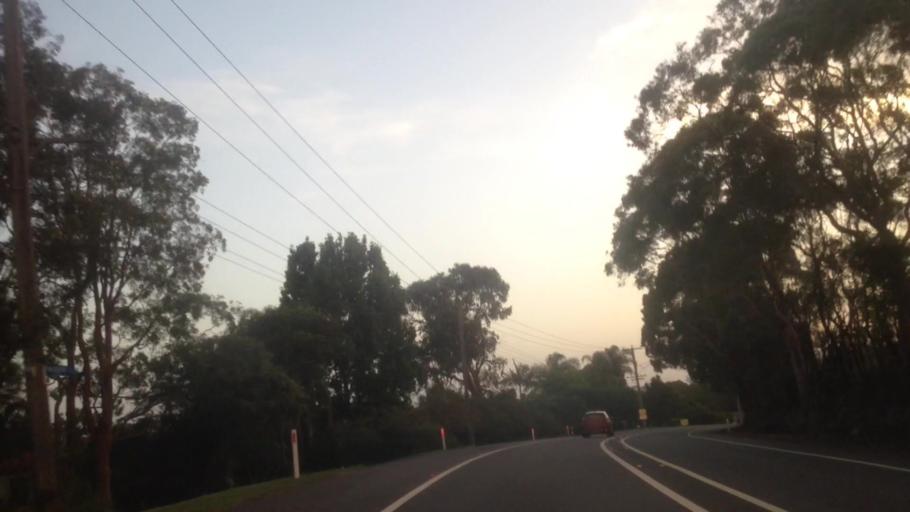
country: AU
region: New South Wales
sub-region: Lake Macquarie Shire
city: Dora Creek
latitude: -33.1031
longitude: 151.5016
